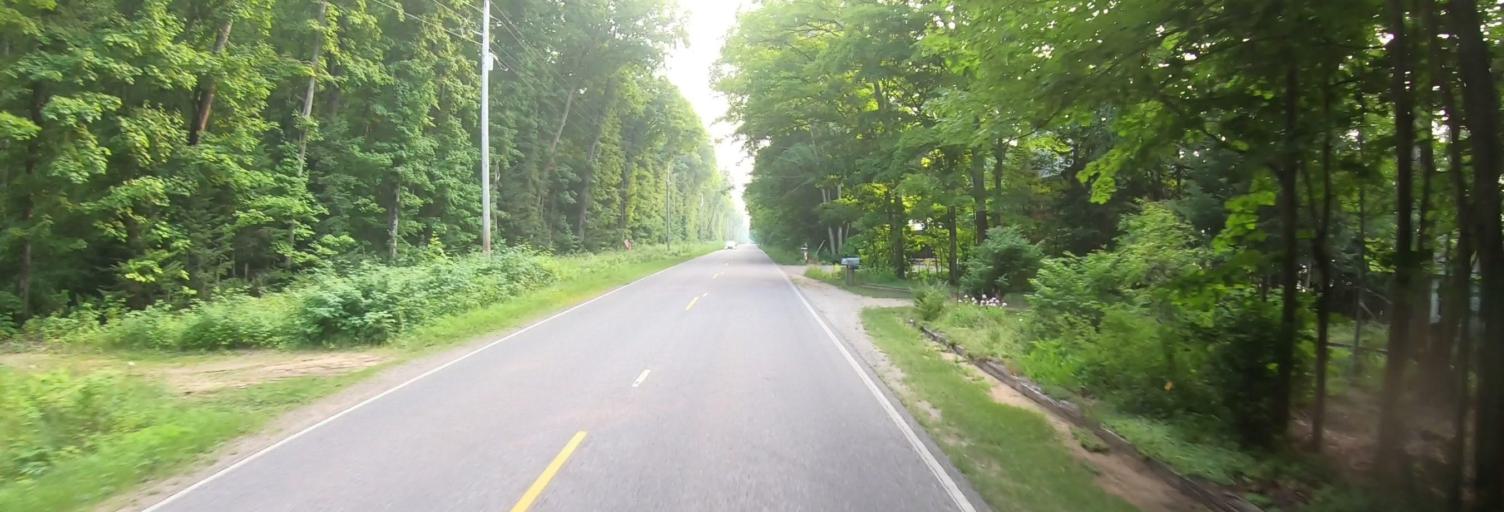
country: US
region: Michigan
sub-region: Chippewa County
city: Sault Ste. Marie
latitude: 46.4744
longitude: -84.7068
